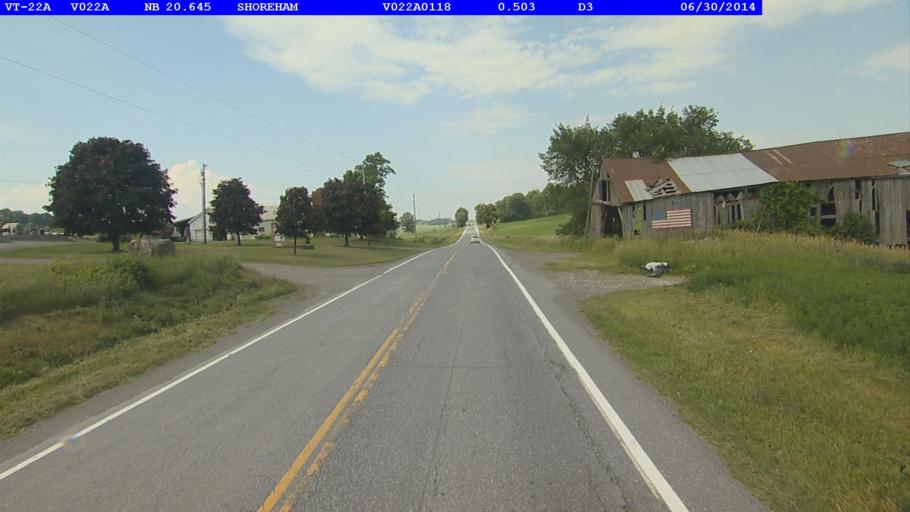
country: US
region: New York
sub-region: Essex County
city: Ticonderoga
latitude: 43.8567
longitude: -73.3093
